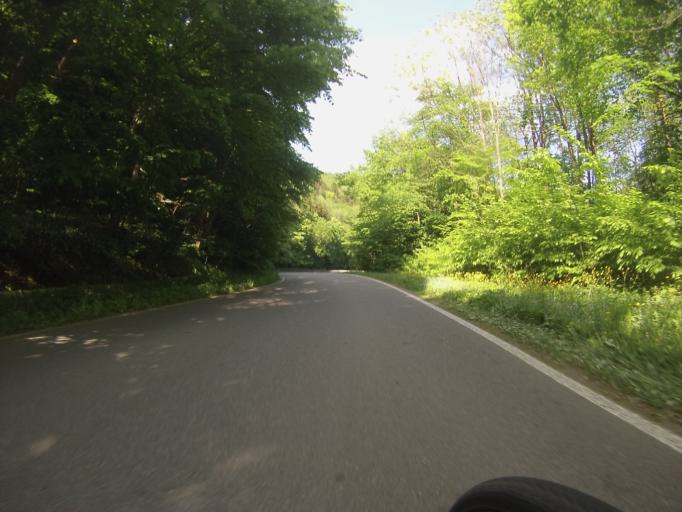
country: CZ
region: South Moravian
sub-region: Okres Blansko
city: Blansko
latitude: 49.3595
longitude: 16.6895
